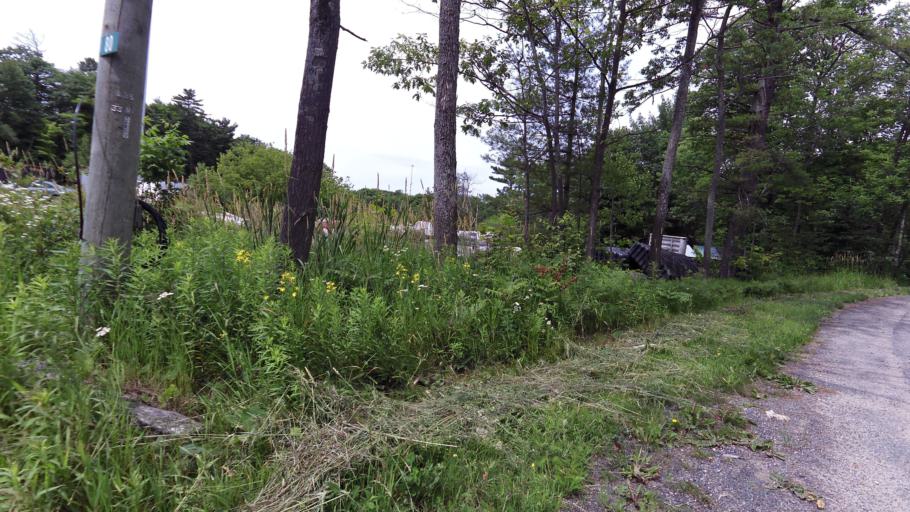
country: CA
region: Ontario
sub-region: Parry Sound District
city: Parry Sound
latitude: 45.3786
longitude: -80.0268
